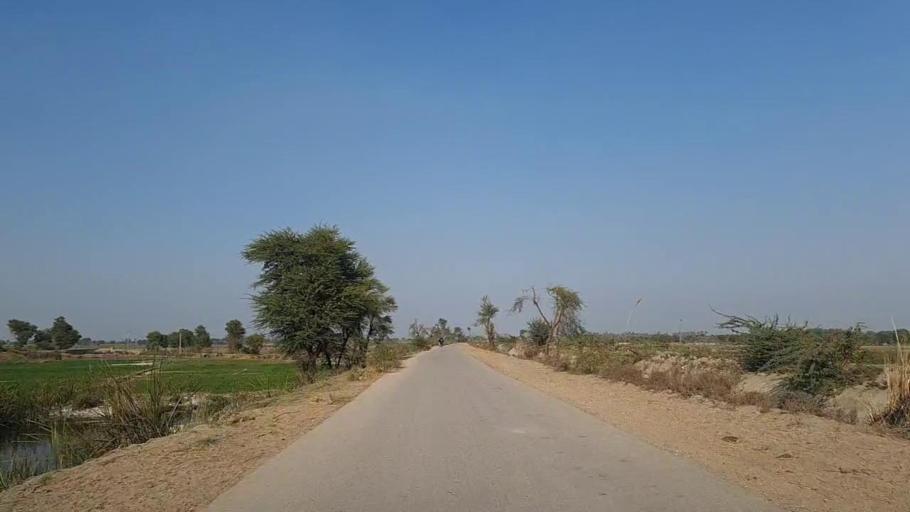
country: PK
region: Sindh
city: Daur
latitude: 26.4268
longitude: 68.2633
